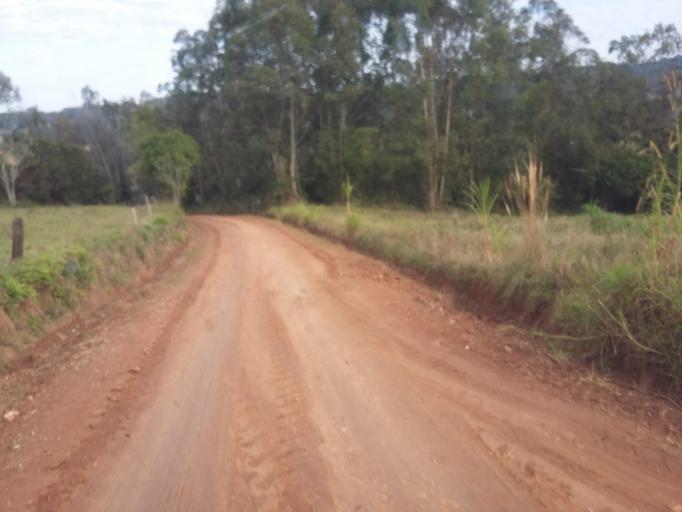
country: BR
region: Rio Grande do Sul
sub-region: Camaqua
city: Camaqua
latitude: -30.7107
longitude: -51.7793
